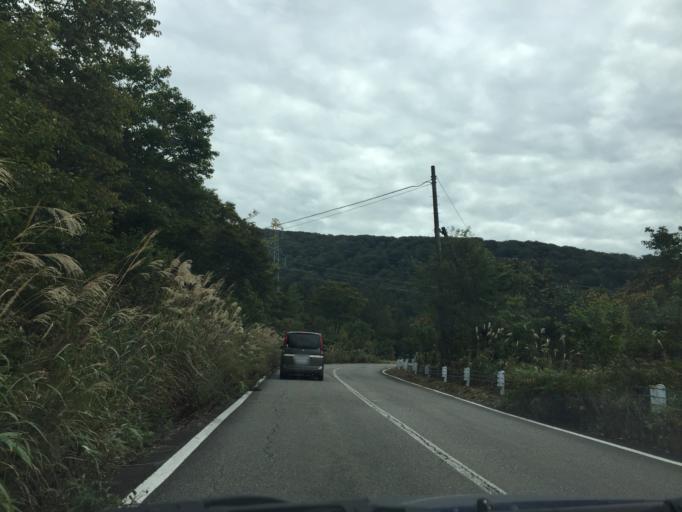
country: JP
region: Fukushima
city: Inawashiro
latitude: 37.6596
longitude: 140.2582
